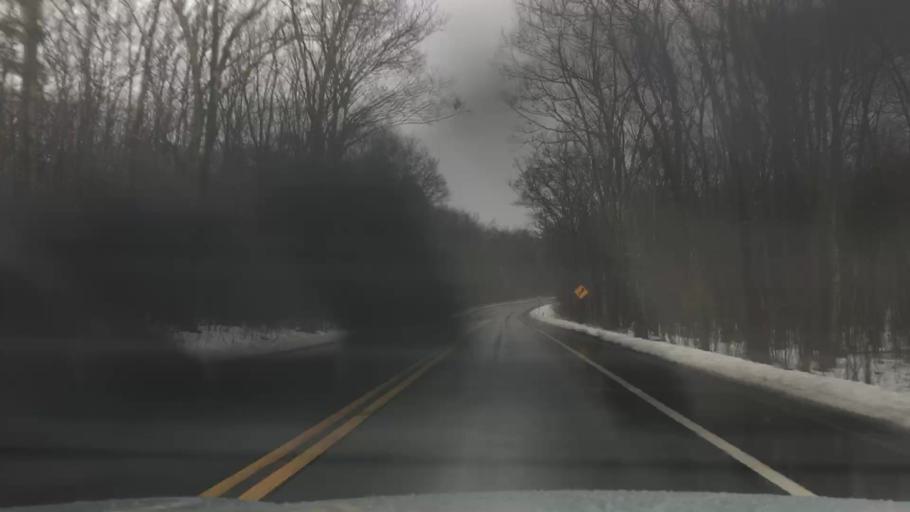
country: US
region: Massachusetts
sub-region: Hampshire County
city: Pelham
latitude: 42.4096
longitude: -72.4027
